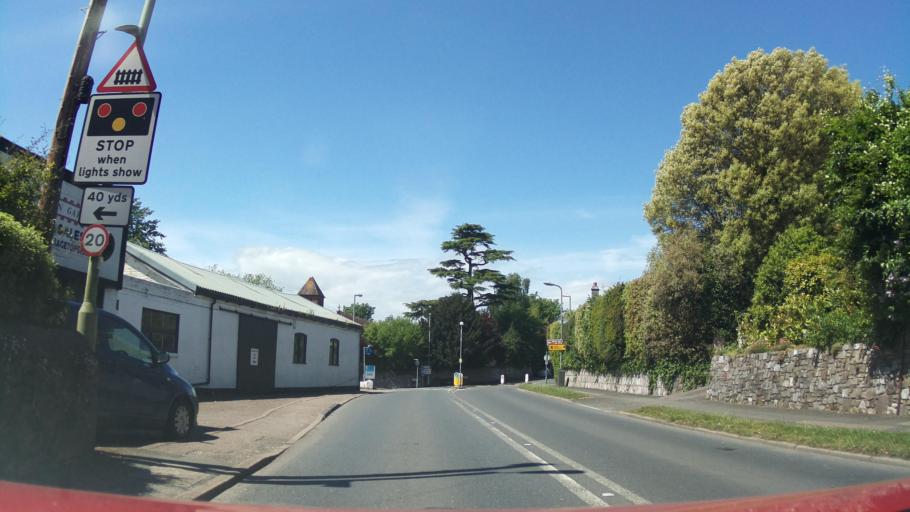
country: GB
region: England
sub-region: Devon
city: Topsham
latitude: 50.6861
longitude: -3.4631
